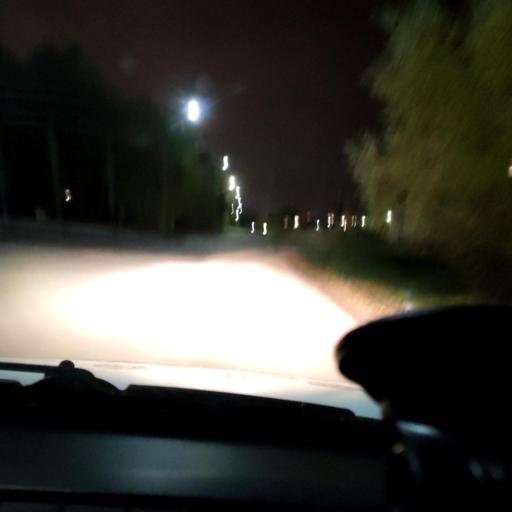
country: RU
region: Perm
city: Kondratovo
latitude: 57.9762
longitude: 56.1111
